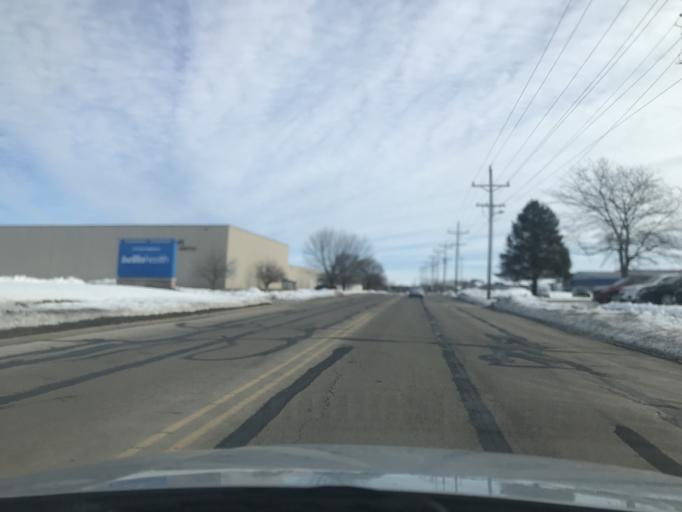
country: US
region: Wisconsin
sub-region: Oconto County
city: Oconto Falls
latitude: 44.8827
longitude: -88.1491
